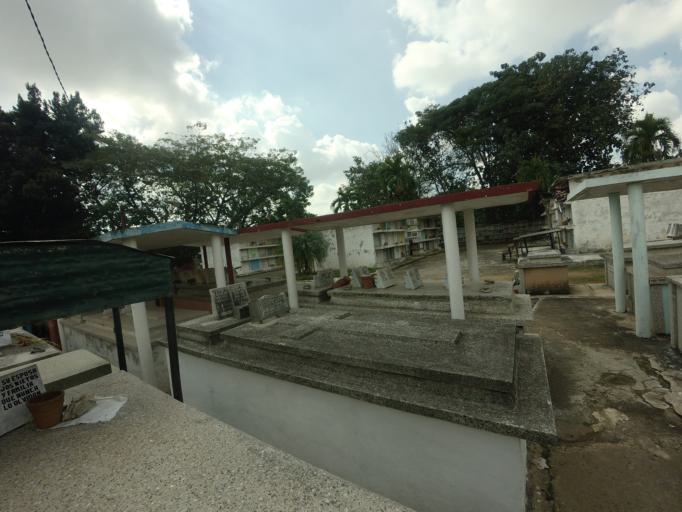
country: CU
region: Artemisa
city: Bauta
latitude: 22.9826
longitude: -82.5522
